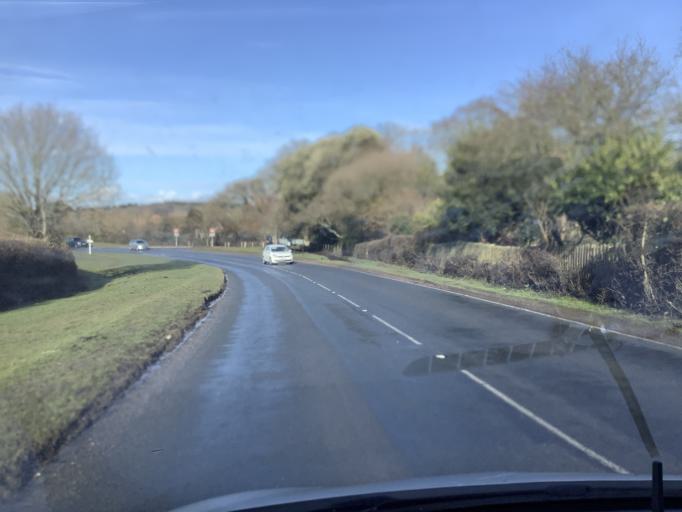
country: GB
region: England
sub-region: Hampshire
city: Hythe
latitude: 50.8148
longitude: -1.4539
